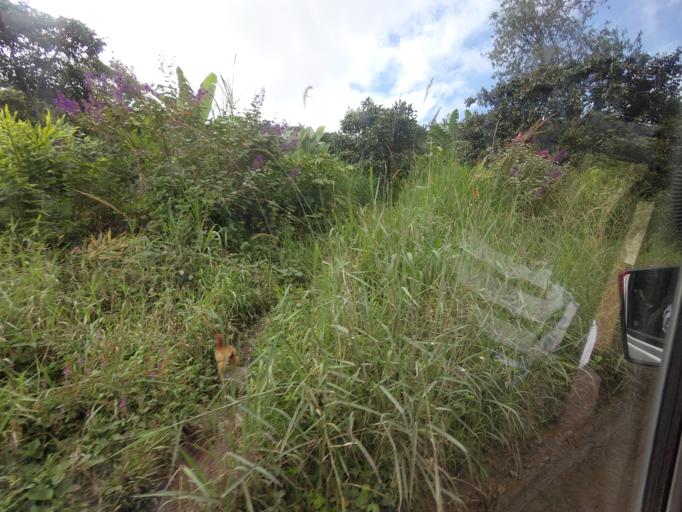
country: CO
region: Huila
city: San Agustin
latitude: 1.9217
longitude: -76.2979
